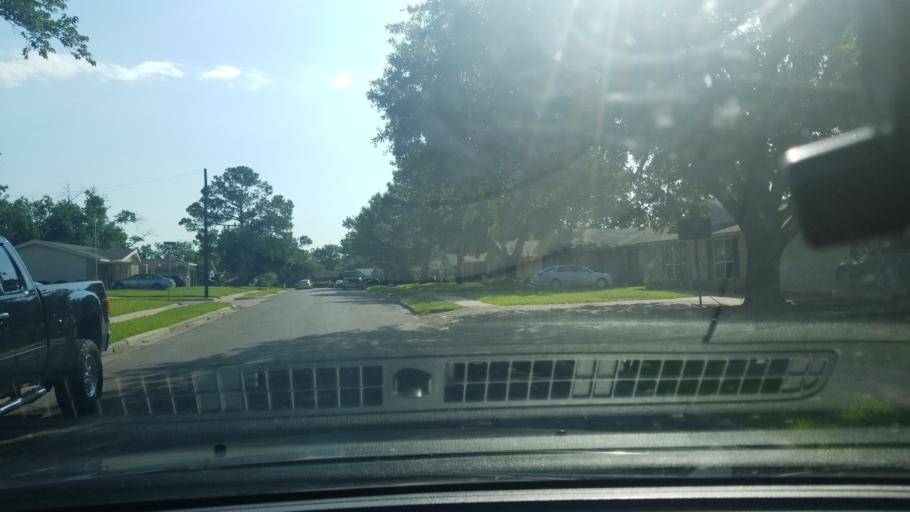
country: US
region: Texas
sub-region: Dallas County
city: Mesquite
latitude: 32.8226
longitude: -96.6342
